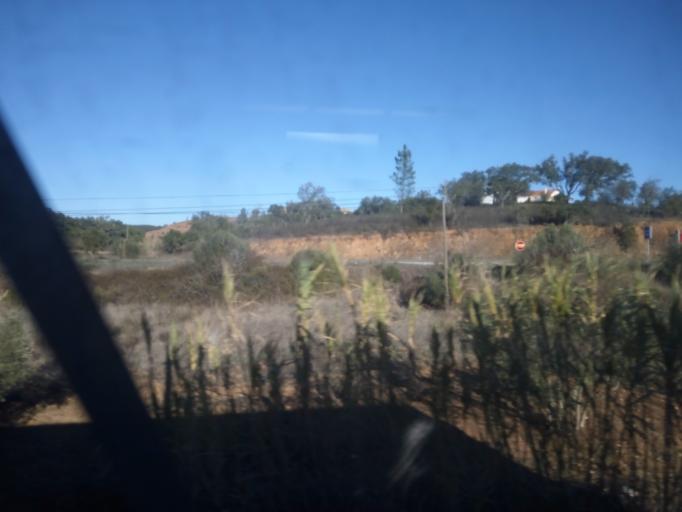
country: PT
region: Faro
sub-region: Silves
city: Sao Bartolomeu de Messines
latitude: 37.3268
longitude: -8.3371
